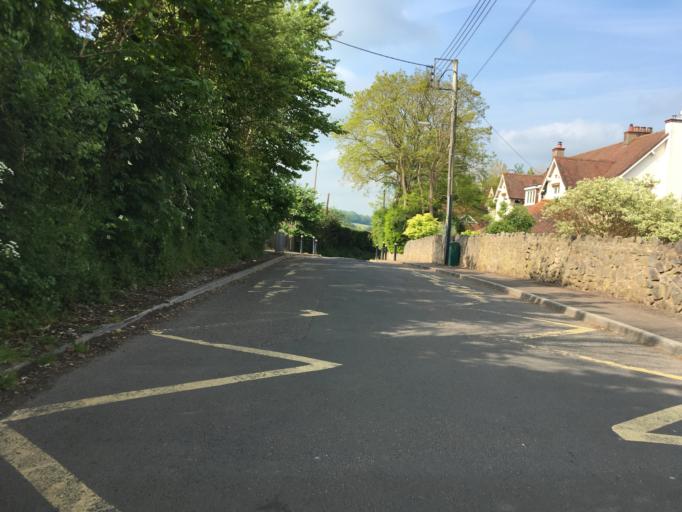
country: GB
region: England
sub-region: North Somerset
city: Nailsea
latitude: 51.4109
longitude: -2.7331
